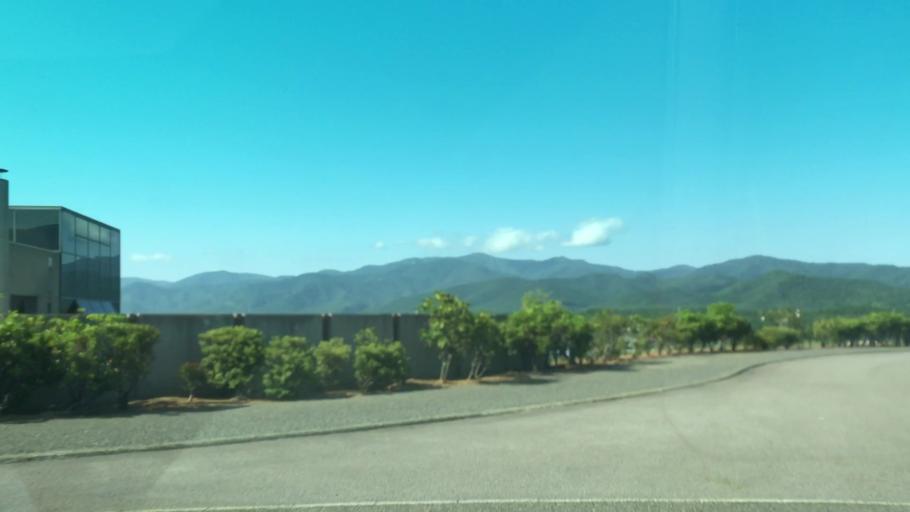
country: JP
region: Hokkaido
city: Iwanai
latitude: 42.9748
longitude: 140.6095
